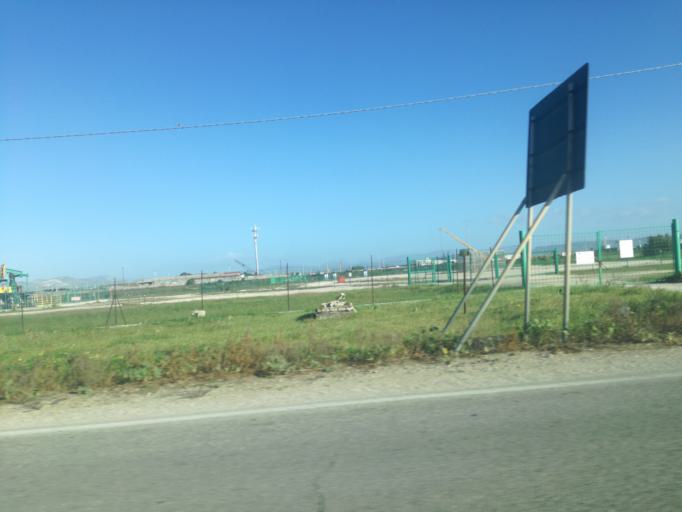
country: IT
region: Sicily
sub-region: Provincia di Caltanissetta
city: Gela
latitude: 37.0587
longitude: 14.2851
